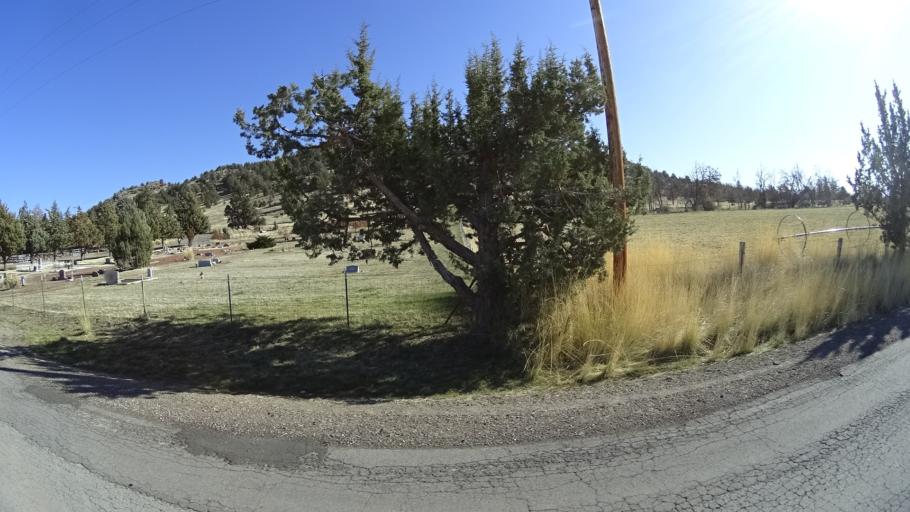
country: US
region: California
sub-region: Siskiyou County
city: Montague
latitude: 41.7085
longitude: -122.3794
